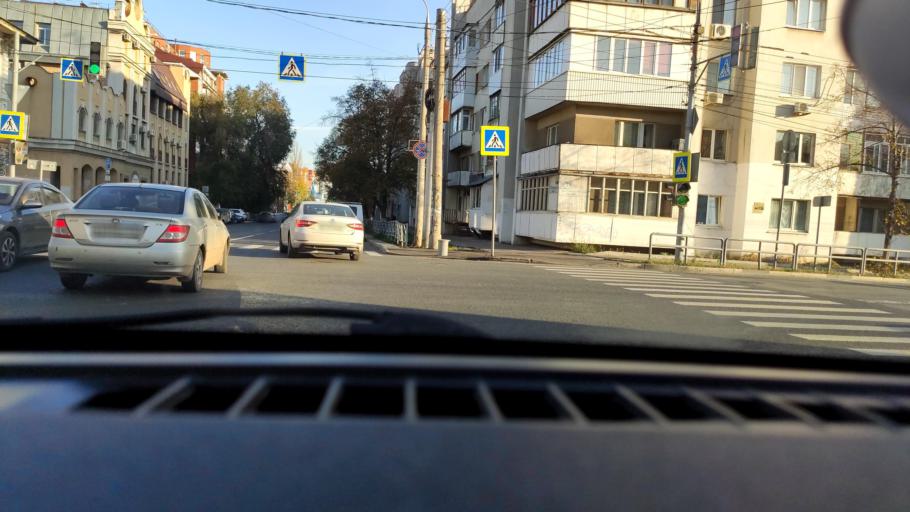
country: RU
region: Samara
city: Samara
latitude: 53.1877
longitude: 50.1015
